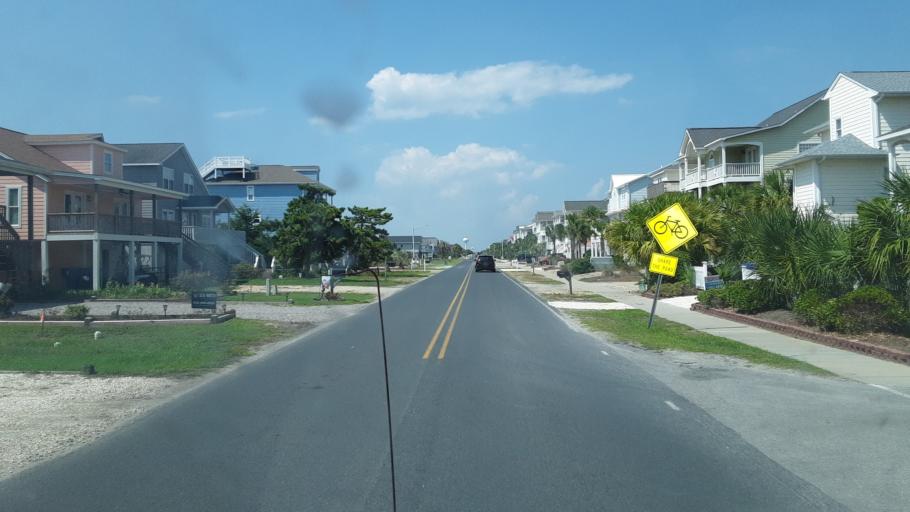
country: US
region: North Carolina
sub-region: Brunswick County
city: Shallotte
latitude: 33.8939
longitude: -78.4146
